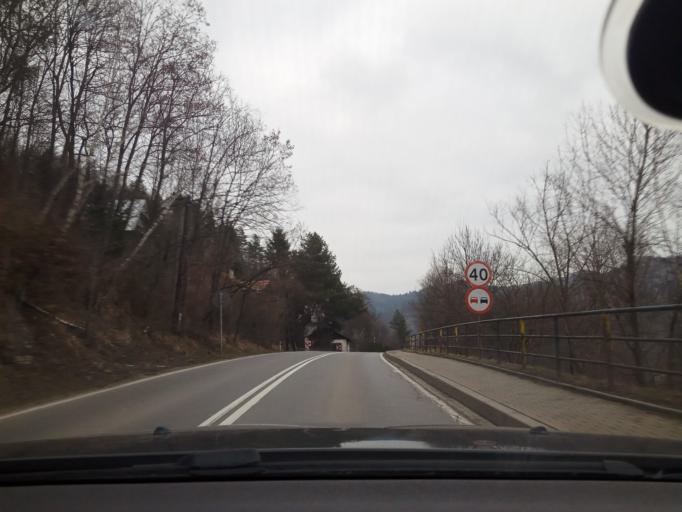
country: PL
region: Lesser Poland Voivodeship
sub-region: Powiat nowosadecki
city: Lacko
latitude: 49.5174
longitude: 20.4031
